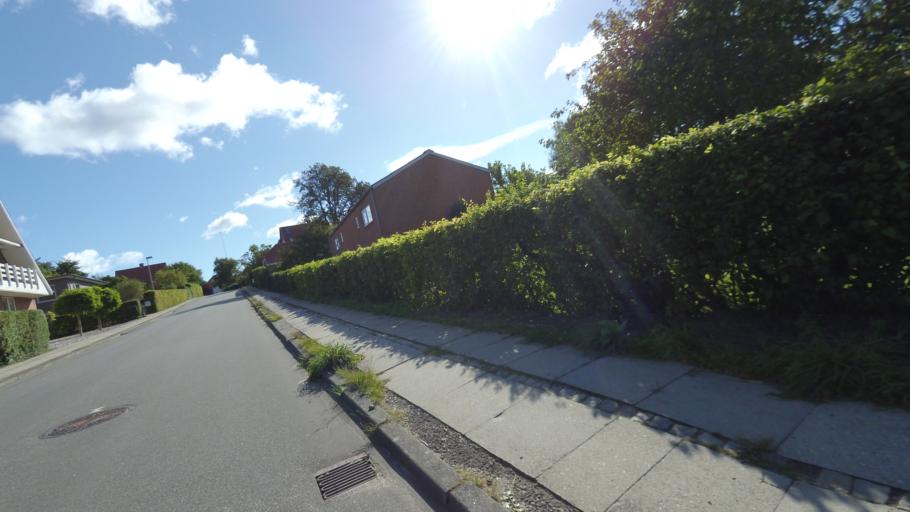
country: DK
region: Central Jutland
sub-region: Arhus Kommune
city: Stavtrup
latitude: 56.1241
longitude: 10.1565
